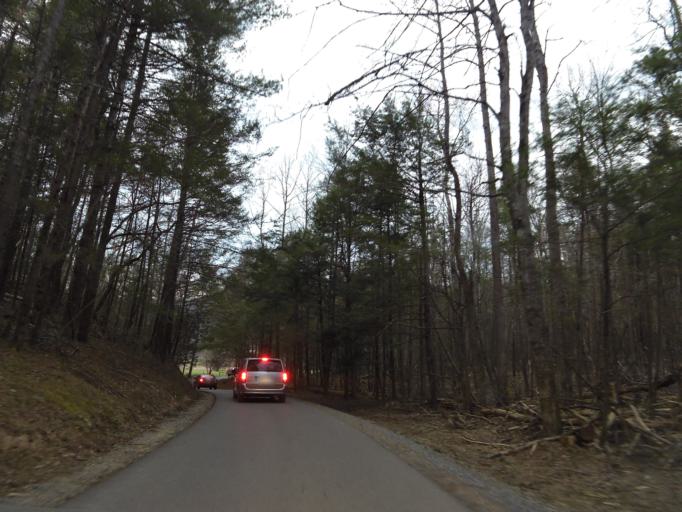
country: US
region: Tennessee
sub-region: Blount County
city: Wildwood
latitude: 35.5912
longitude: -83.7976
